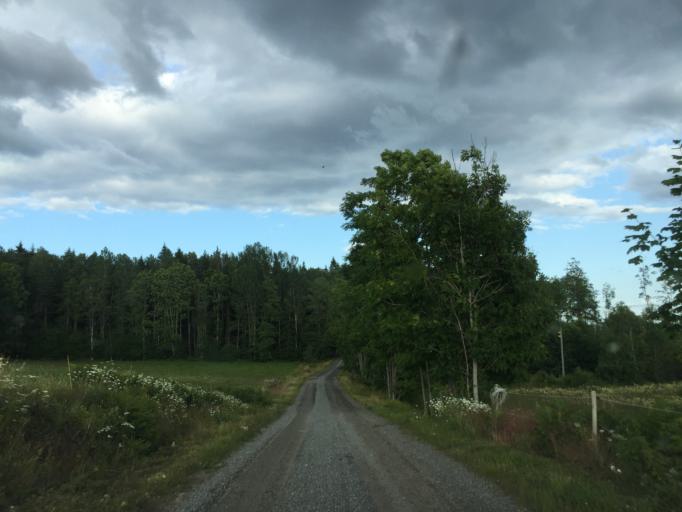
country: SE
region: OEstergoetland
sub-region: Motala Kommun
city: Ryd
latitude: 58.7132
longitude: 15.0281
